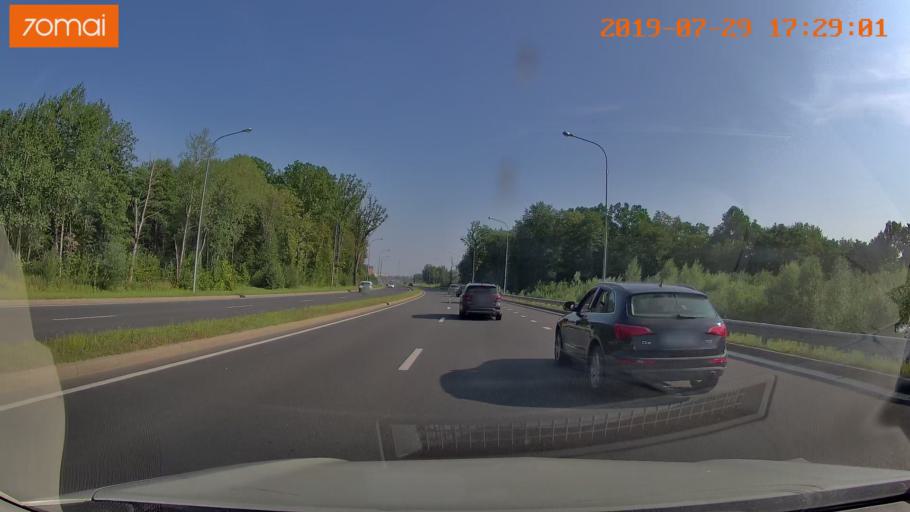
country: RU
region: Kaliningrad
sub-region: Gorod Kaliningrad
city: Kaliningrad
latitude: 54.7582
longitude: 20.4709
